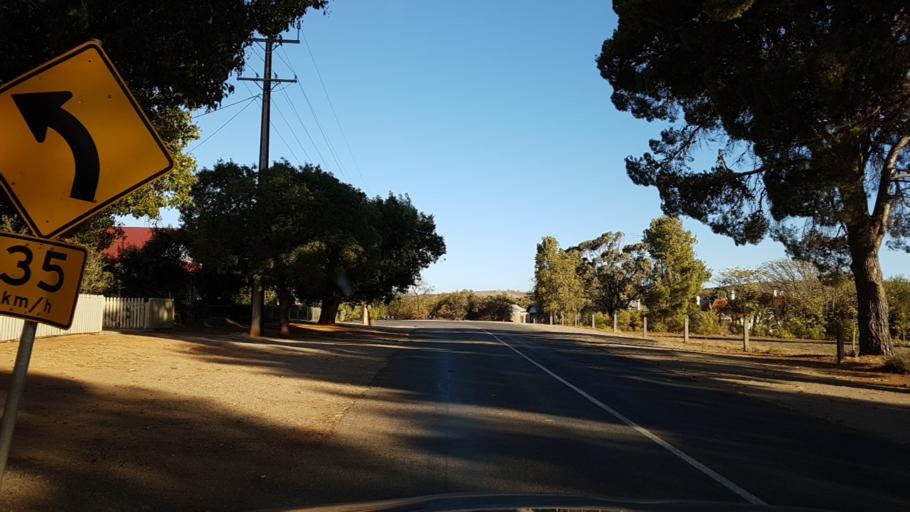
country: AU
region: South Australia
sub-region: Clare and Gilbert Valleys
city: Clare
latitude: -33.6711
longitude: 138.9343
